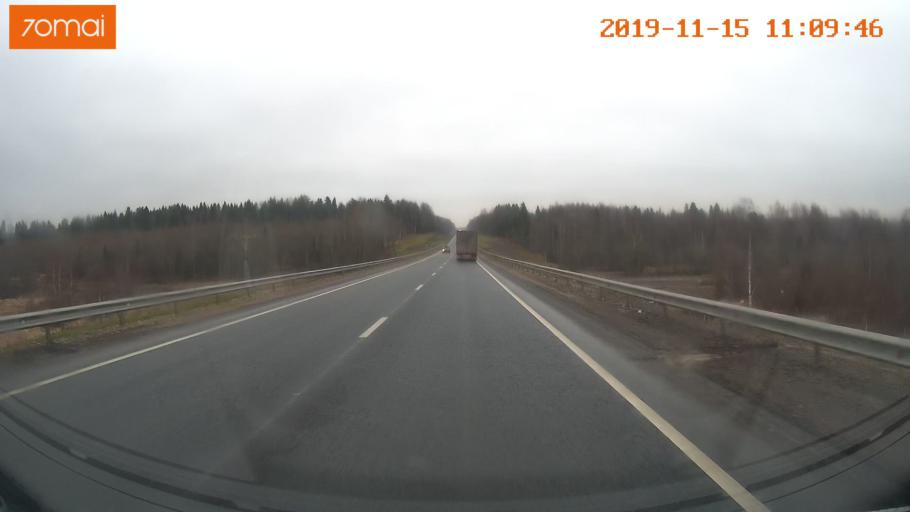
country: RU
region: Vologda
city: Chebsara
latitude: 59.1206
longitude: 39.1058
